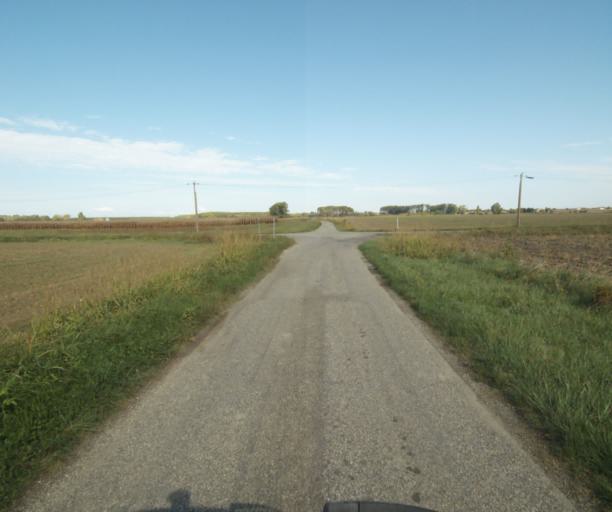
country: FR
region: Midi-Pyrenees
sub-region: Departement du Tarn-et-Garonne
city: Finhan
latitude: 43.8894
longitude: 1.2208
